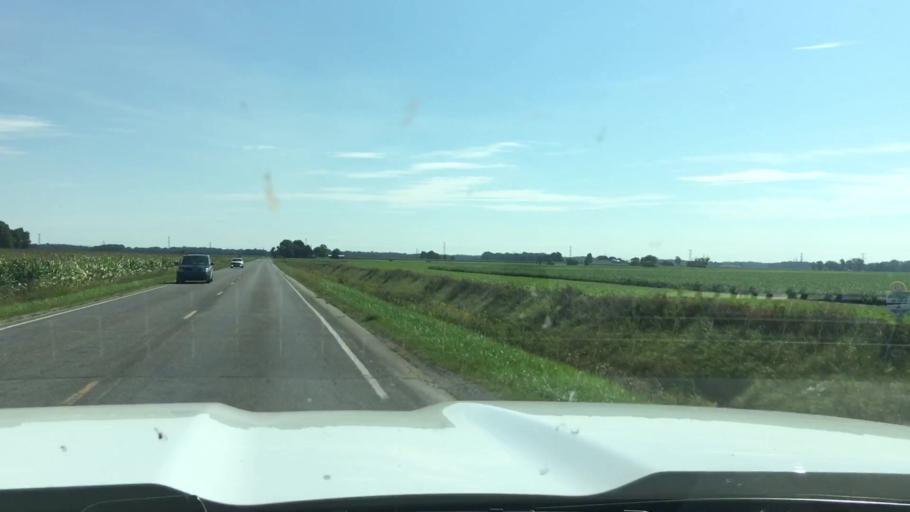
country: US
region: Michigan
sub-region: Saginaw County
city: Freeland
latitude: 43.5252
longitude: -84.2090
